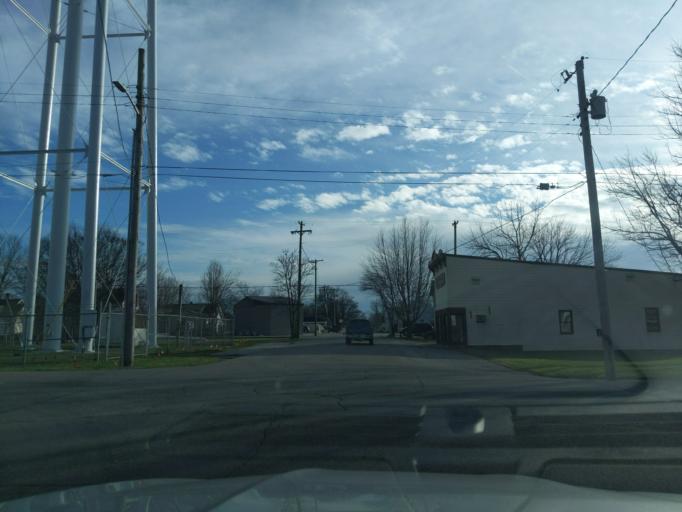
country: US
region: Indiana
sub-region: Decatur County
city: Westport
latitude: 39.1769
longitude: -85.5729
